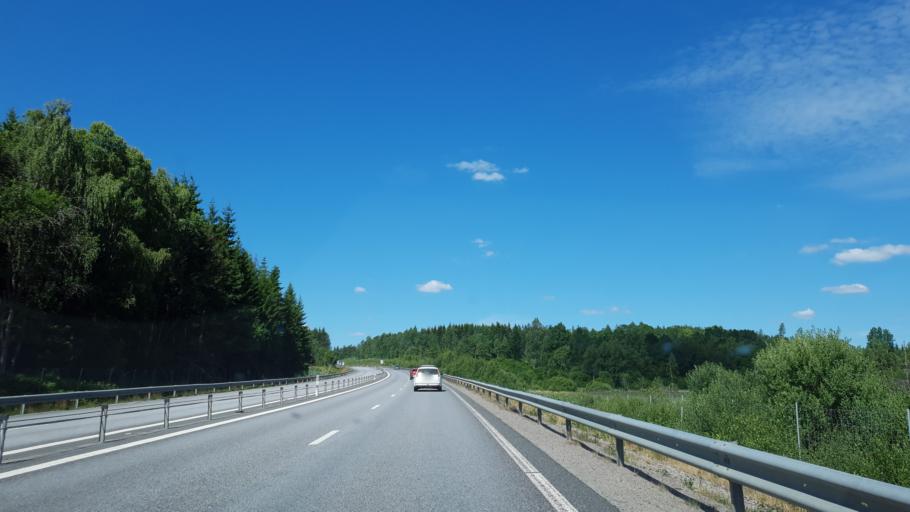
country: SE
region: Kronoberg
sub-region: Vaxjo Kommun
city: Gemla
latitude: 56.9189
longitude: 14.6117
